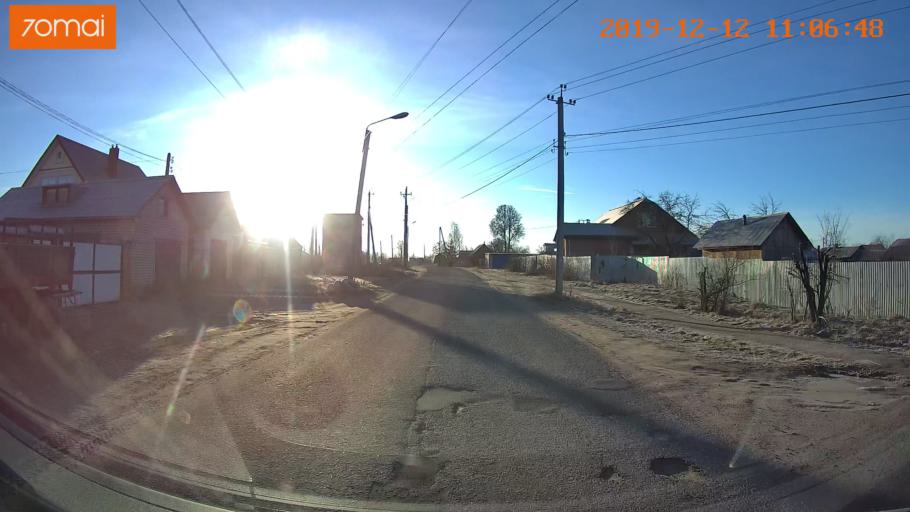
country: RU
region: Ivanovo
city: Kokhma
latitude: 56.9414
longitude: 41.0884
